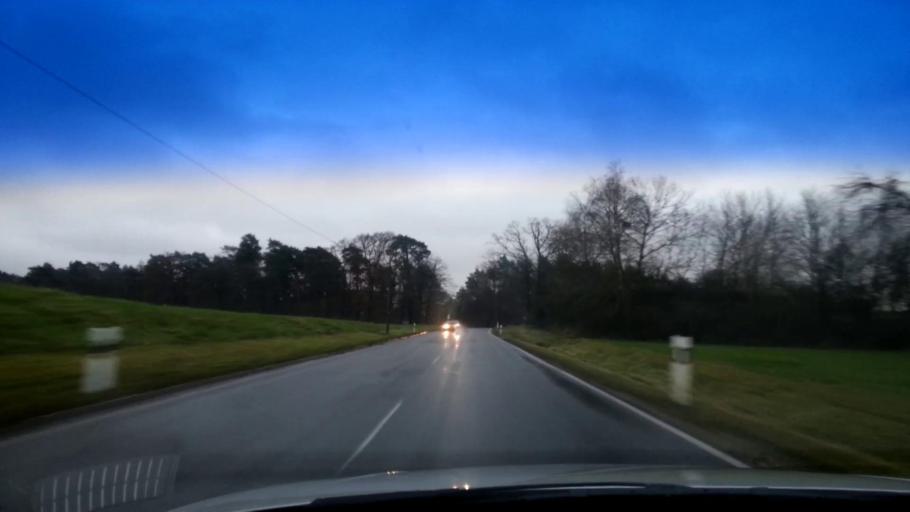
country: DE
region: Bavaria
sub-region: Upper Franconia
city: Lauter
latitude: 49.9638
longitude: 10.8047
